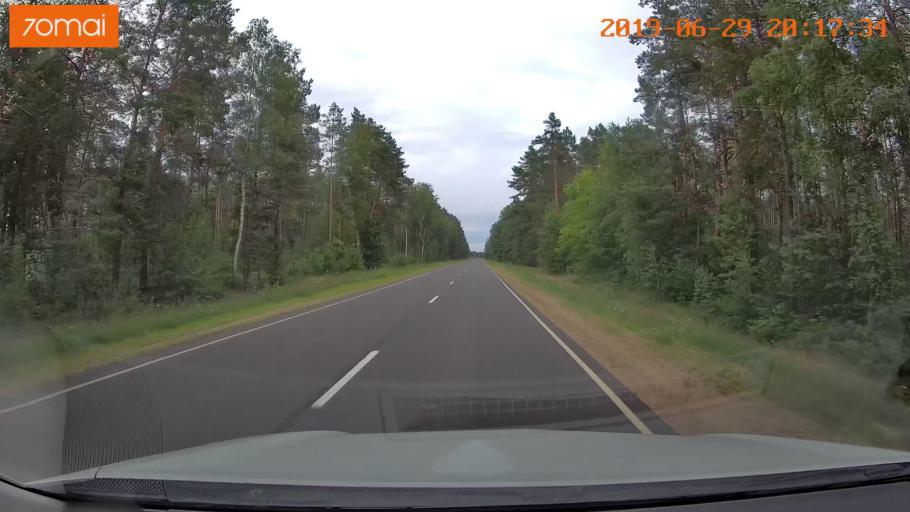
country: BY
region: Brest
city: Asnyezhytsy
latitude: 52.3889
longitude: 26.2189
